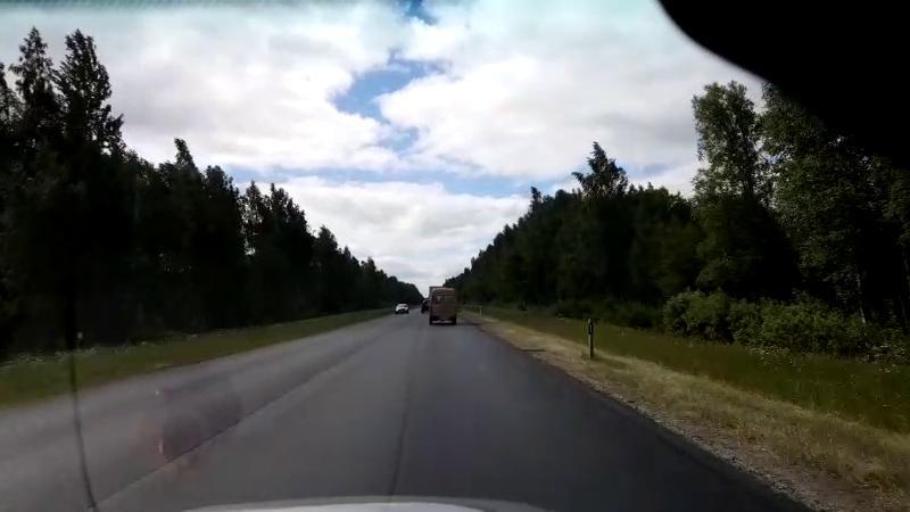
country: LV
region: Salacgrivas
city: Ainazi
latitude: 57.9593
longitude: 24.4426
